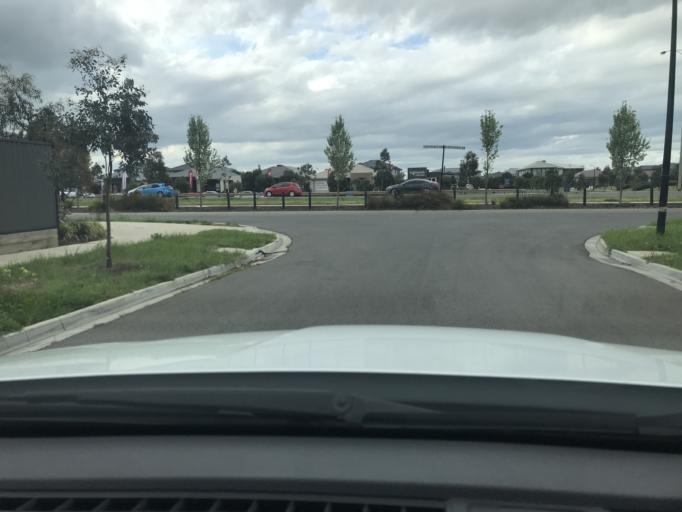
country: AU
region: Victoria
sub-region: Hume
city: Roxburgh Park
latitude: -37.5920
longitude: 144.8929
